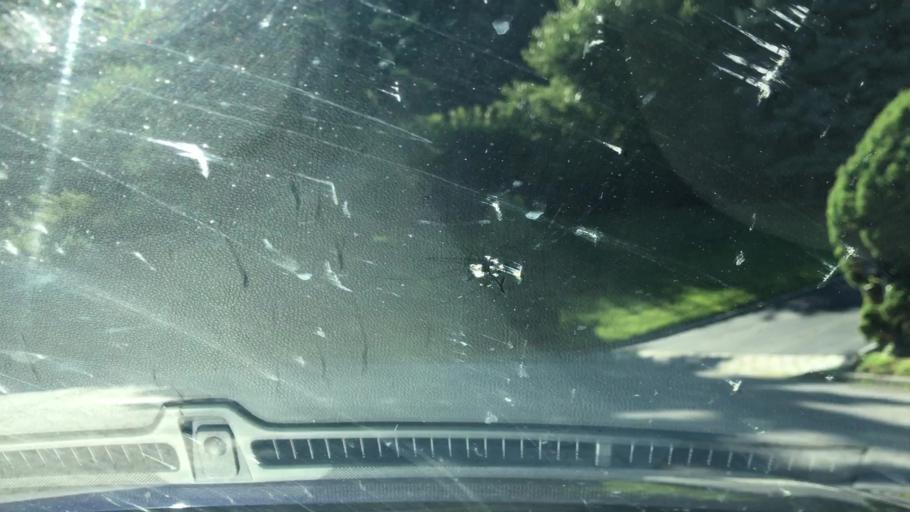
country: US
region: New York
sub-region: Westchester County
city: Hawthorne
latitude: 41.1086
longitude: -73.7813
